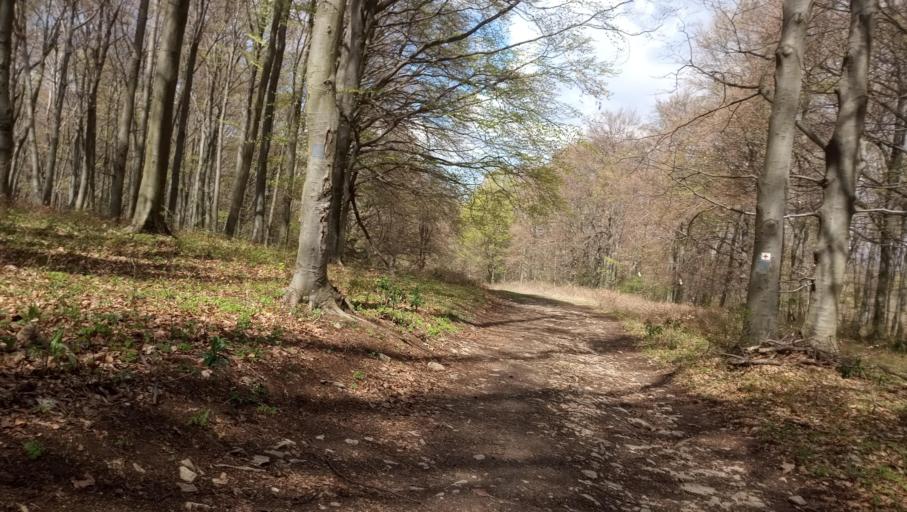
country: HU
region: Veszprem
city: Herend
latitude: 47.2004
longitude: 17.7556
